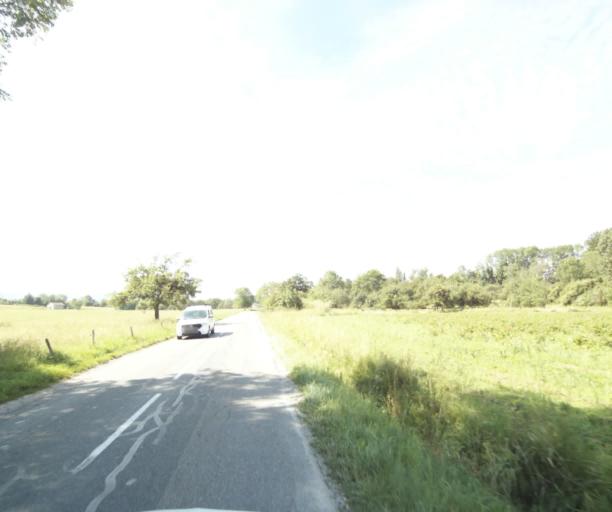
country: FR
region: Rhone-Alpes
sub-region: Departement de la Haute-Savoie
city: Margencel
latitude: 46.3347
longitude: 6.4188
